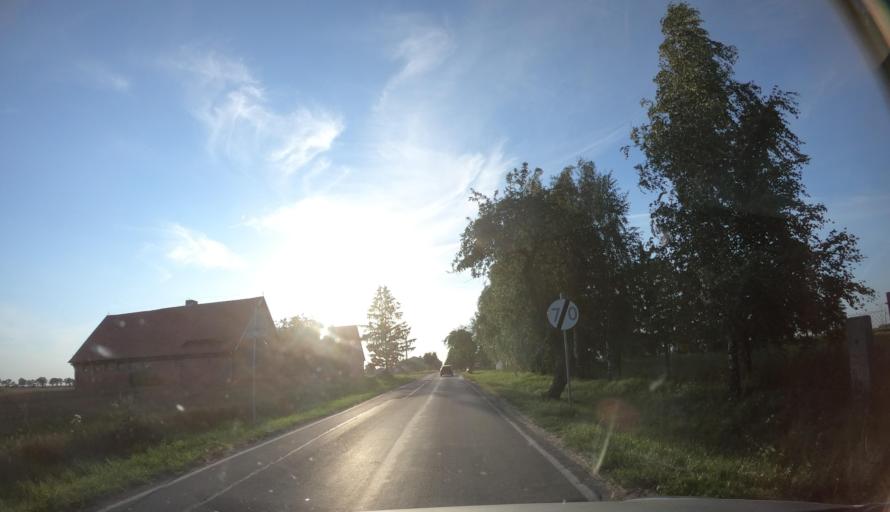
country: PL
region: Kujawsko-Pomorskie
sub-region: Powiat swiecki
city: Pruszcz
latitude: 53.2470
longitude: 18.2029
